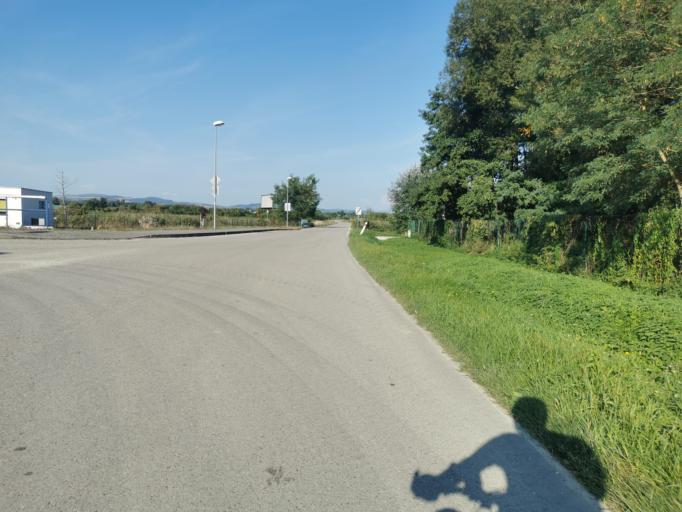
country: SK
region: Trnavsky
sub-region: Okres Senica
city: Senica
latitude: 48.6592
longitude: 17.3103
